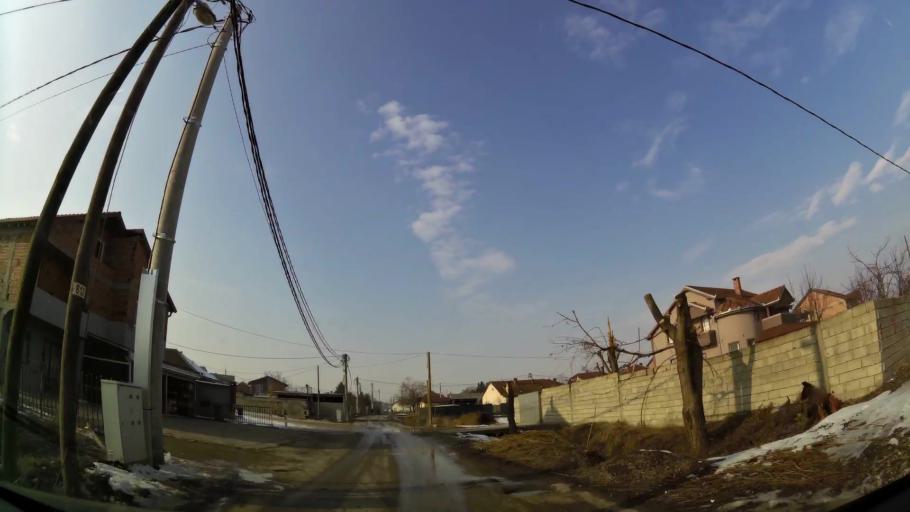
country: MK
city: Creshevo
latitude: 42.0196
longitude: 21.5042
